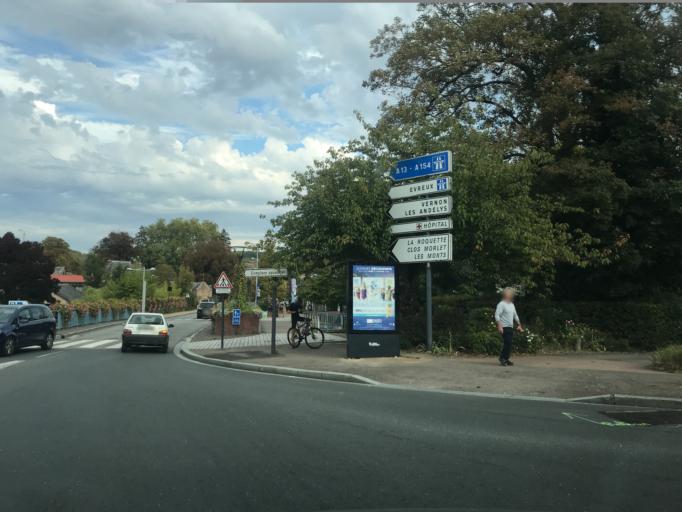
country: FR
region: Haute-Normandie
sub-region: Departement de l'Eure
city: Louviers
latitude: 49.2101
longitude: 1.1708
